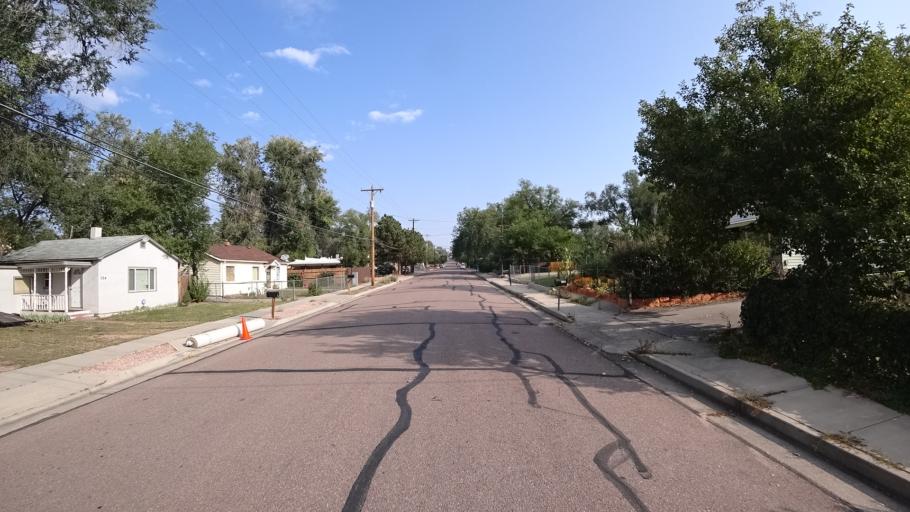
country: US
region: Colorado
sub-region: El Paso County
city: Colorado Springs
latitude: 38.8426
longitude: -104.7804
